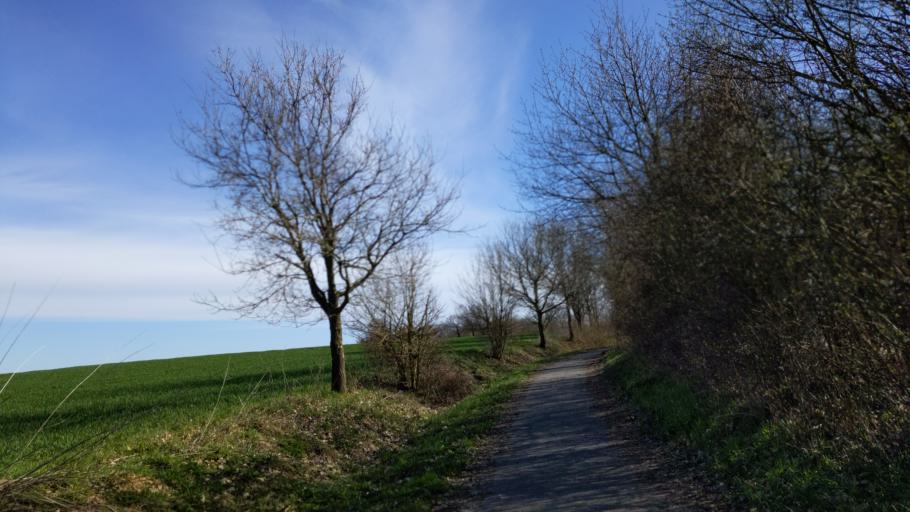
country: DE
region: Schleswig-Holstein
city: Susel
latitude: 54.1104
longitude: 10.6989
